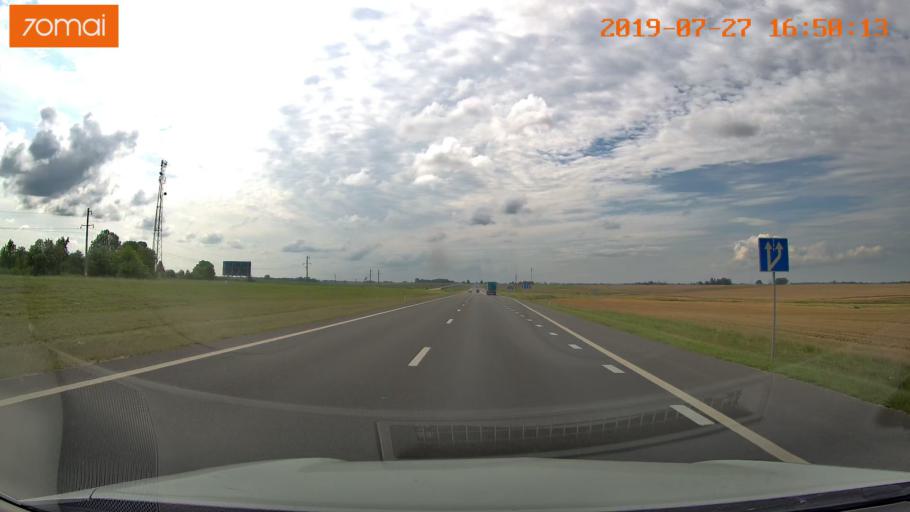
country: RU
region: Kaliningrad
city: Gvardeysk
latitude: 54.6765
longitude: 20.9194
